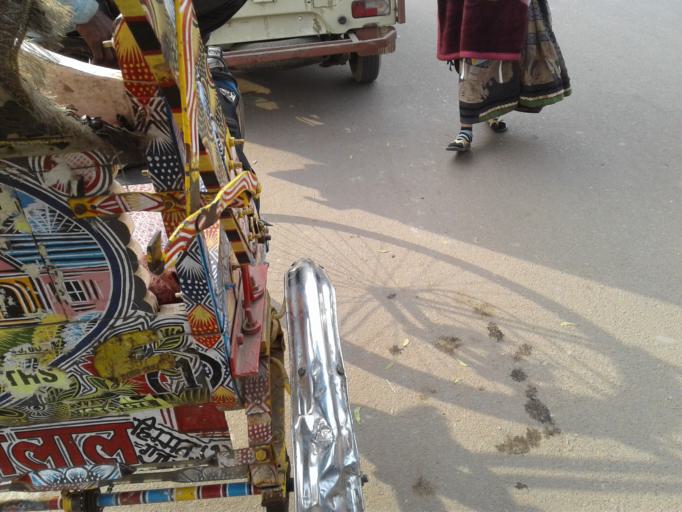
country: IN
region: Uttar Pradesh
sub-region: Allahabad
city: Allahabad
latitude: 25.4497
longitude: 81.8397
